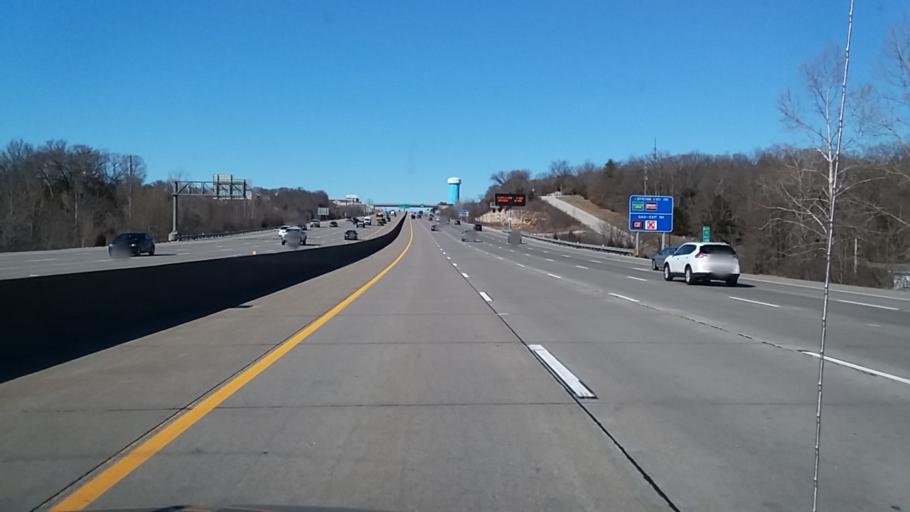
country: US
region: Missouri
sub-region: Jefferson County
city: Arnold
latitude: 38.4257
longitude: -90.3851
